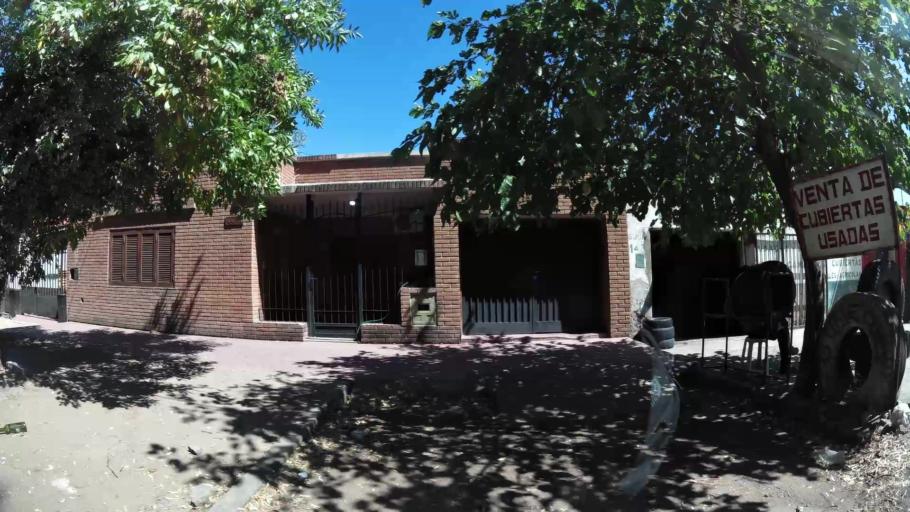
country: AR
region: San Luis
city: San Luis
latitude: -33.2902
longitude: -66.3294
